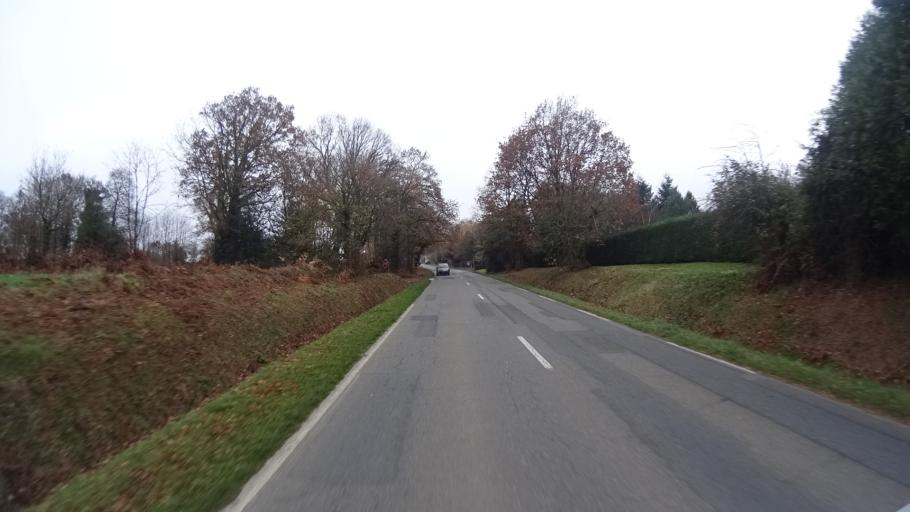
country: FR
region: Brittany
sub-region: Departement d'Ille-et-Vilaine
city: Redon
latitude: 47.6688
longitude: -2.0807
